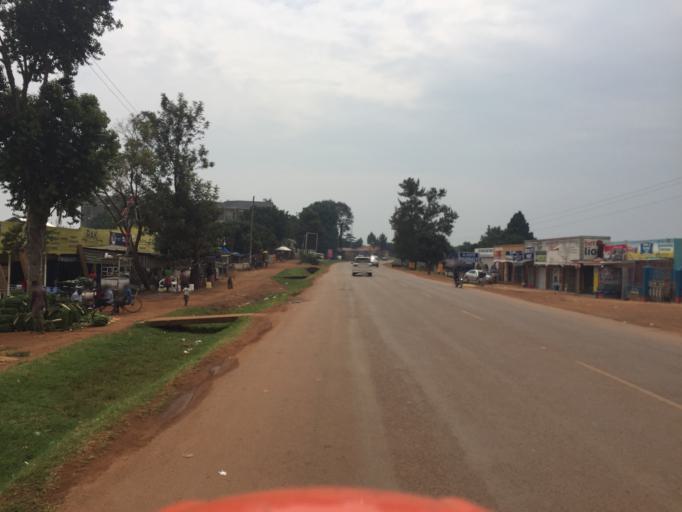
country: UG
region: Central Region
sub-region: Wakiso District
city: Kajansi
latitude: 0.1491
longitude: 32.5457
